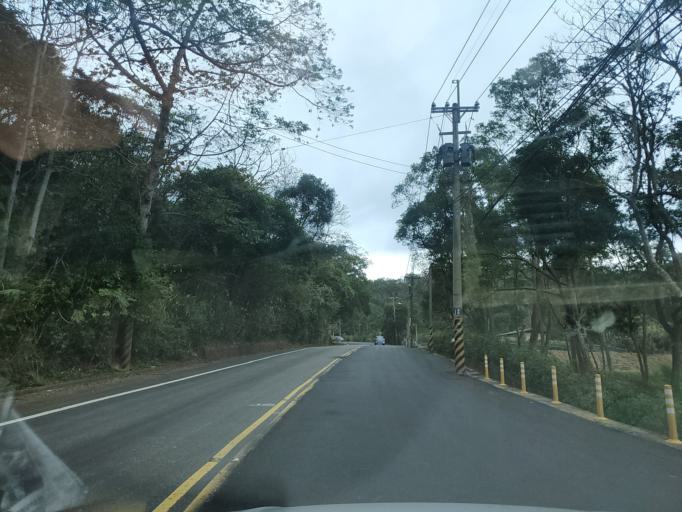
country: TW
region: Taiwan
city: Fengyuan
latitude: 24.3737
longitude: 120.7690
